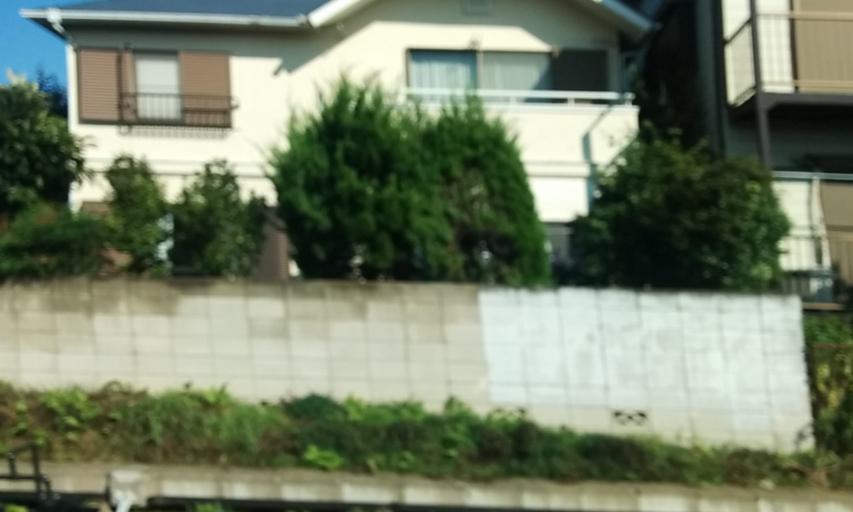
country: JP
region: Tokyo
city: Nishi-Tokyo-shi
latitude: 35.7291
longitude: 139.5585
